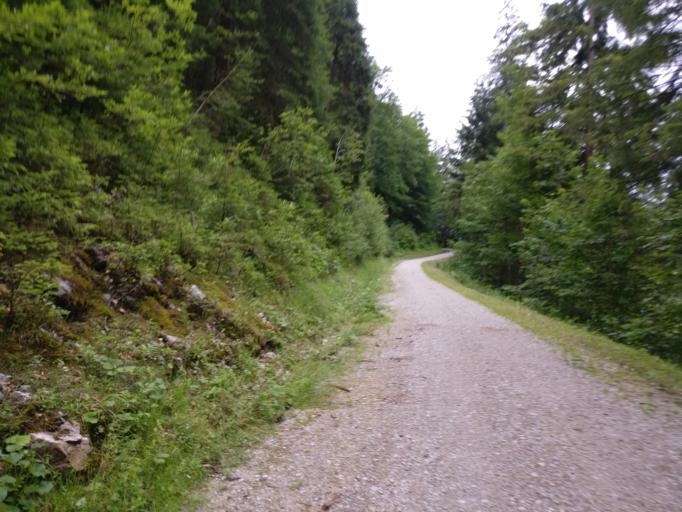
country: AT
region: Tyrol
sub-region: Politischer Bezirk Kitzbuhel
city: Hochfilzen
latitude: 47.4952
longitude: 12.6088
